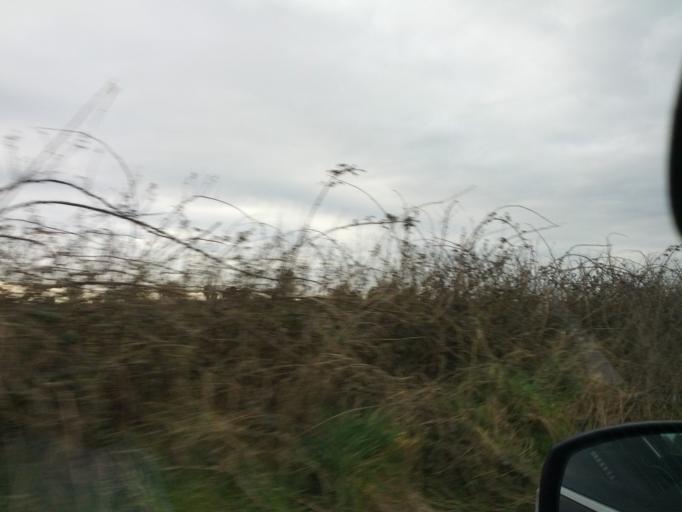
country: IE
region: Connaught
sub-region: County Galway
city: Gort
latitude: 53.1543
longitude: -8.8492
